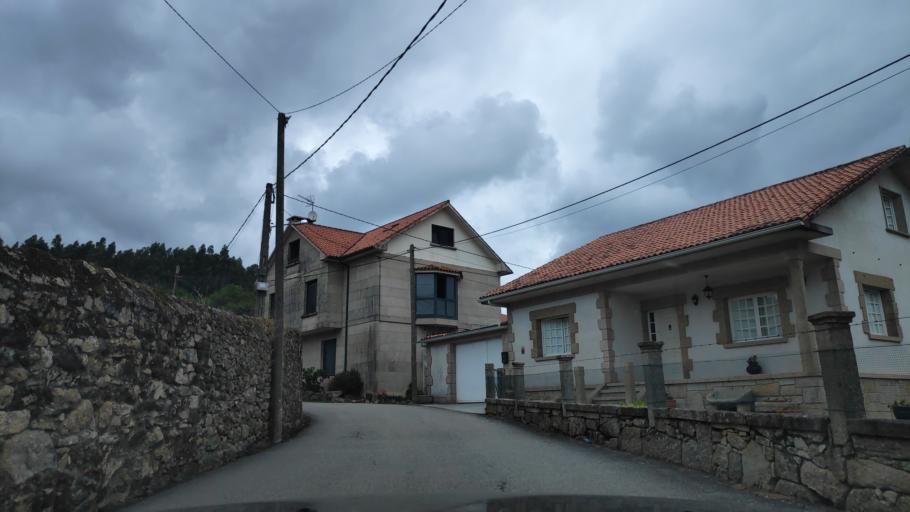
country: ES
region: Galicia
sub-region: Provincia da Coruna
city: Padron
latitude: 42.7341
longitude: -8.6653
